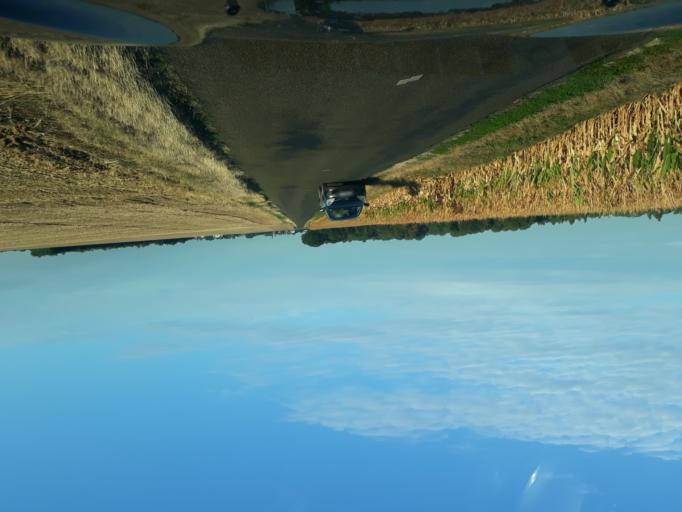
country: FR
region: Centre
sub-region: Departement du Loir-et-Cher
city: Ouzouer-le-Marche
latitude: 47.9553
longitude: 1.5564
